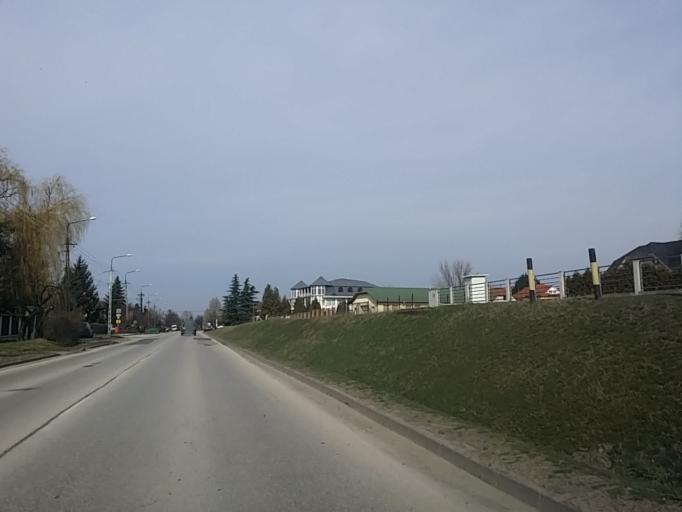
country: HU
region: Pest
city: Fot
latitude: 47.6208
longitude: 19.1895
